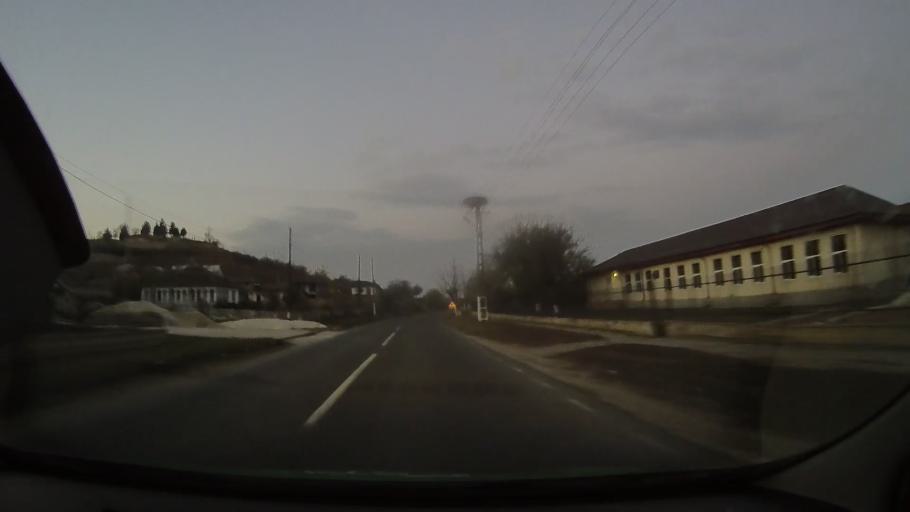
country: RO
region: Constanta
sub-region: Comuna Ion Corvin
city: Ion Corvin
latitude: 44.0972
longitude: 27.7548
